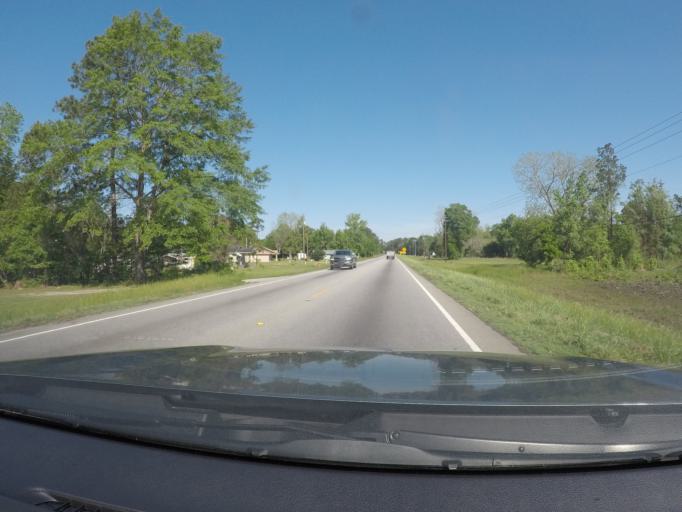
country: US
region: Georgia
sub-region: Chatham County
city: Bloomingdale
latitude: 32.1867
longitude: -81.4021
